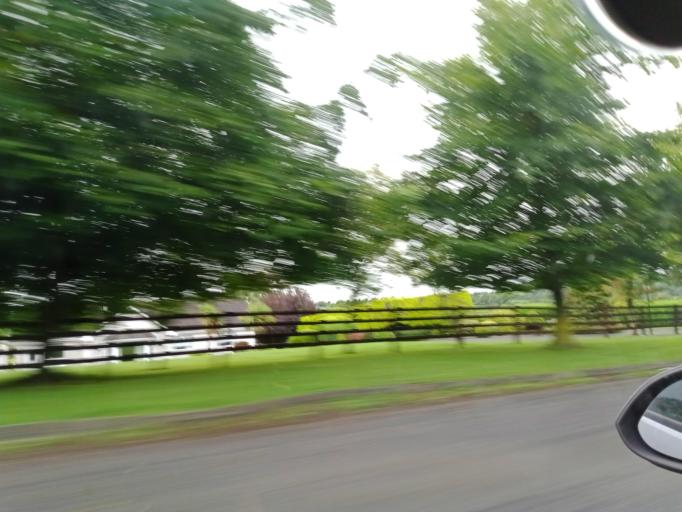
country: IE
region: Leinster
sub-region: Kilkenny
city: Castlecomer
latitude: 52.7561
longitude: -7.2316
